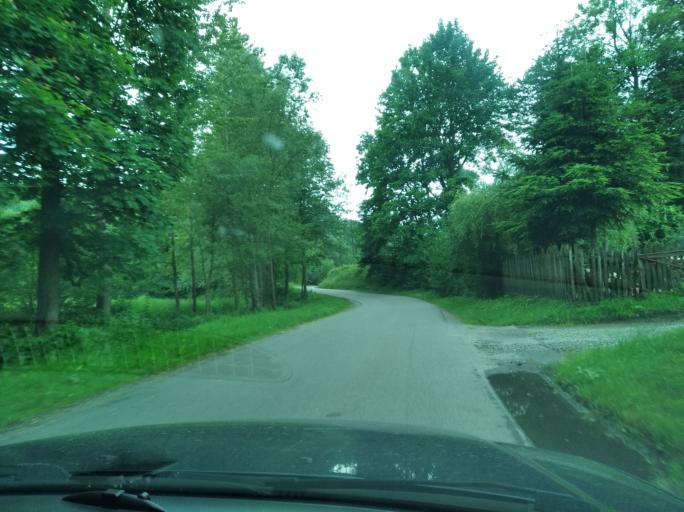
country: PL
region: Subcarpathian Voivodeship
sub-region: Powiat przemyski
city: Nienadowa
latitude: 49.8429
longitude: 22.4143
